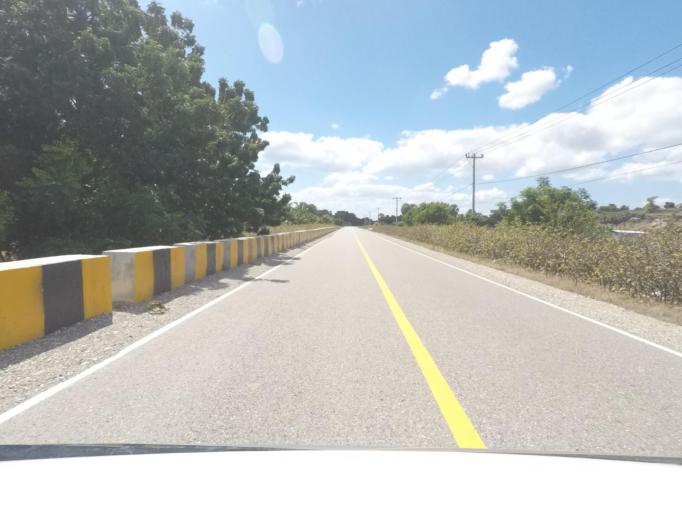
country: TL
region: Baucau
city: Baucau
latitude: -8.4347
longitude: 126.6713
